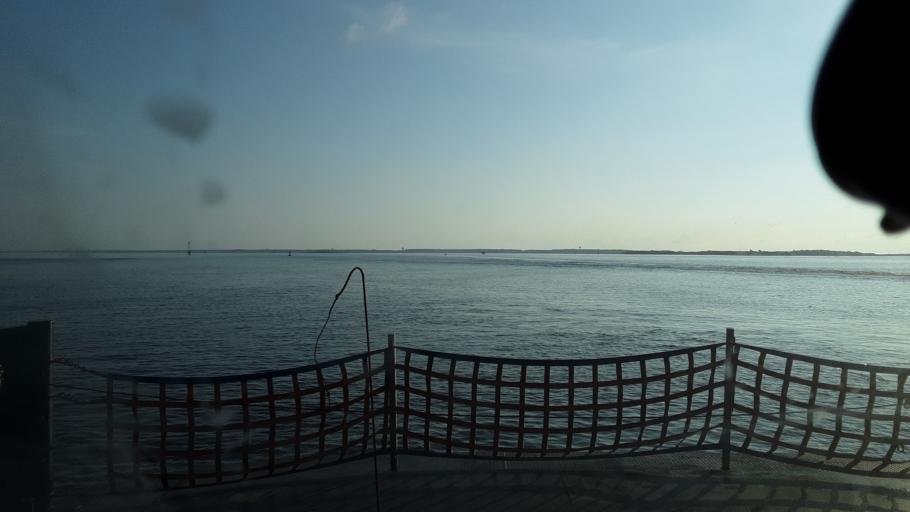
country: US
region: North Carolina
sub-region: New Hanover County
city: Kure Beach
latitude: 33.9544
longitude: -77.9599
